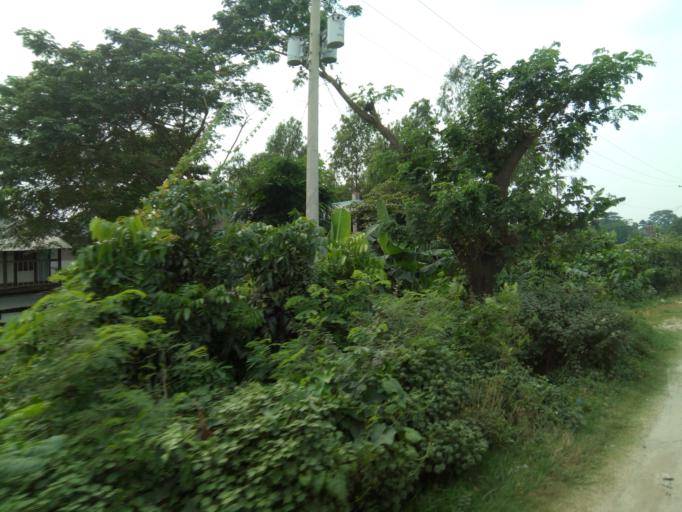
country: BD
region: Dhaka
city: Dohar
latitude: 23.5517
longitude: 90.3000
